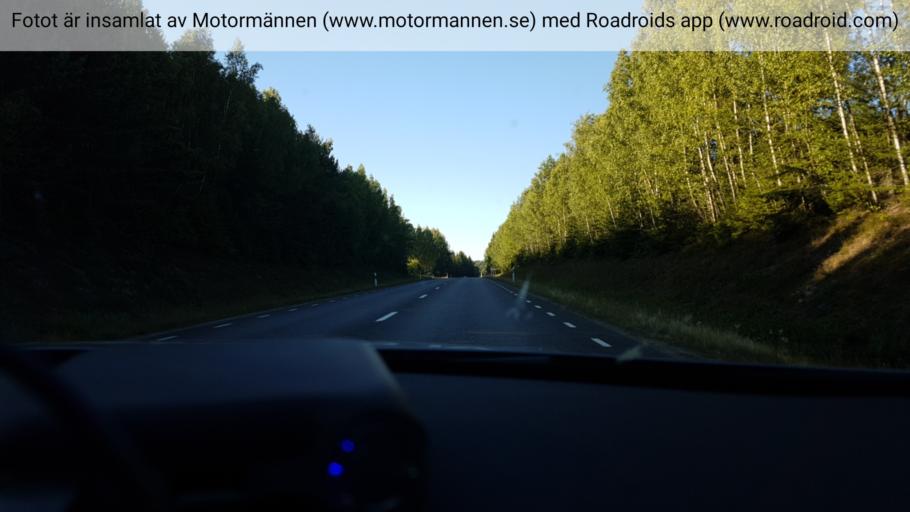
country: SE
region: Joenkoeping
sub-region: Habo Kommun
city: Habo
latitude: 57.9736
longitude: 14.1053
